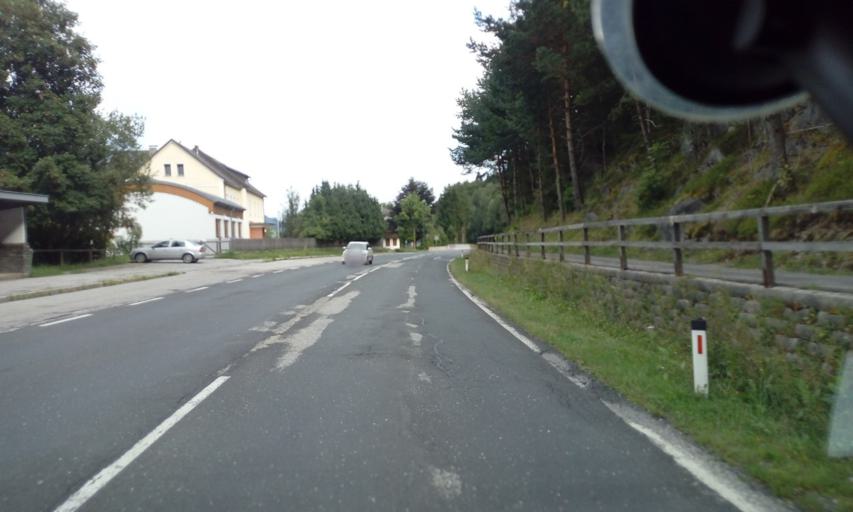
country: AT
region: Carinthia
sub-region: Politischer Bezirk Villach Land
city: Fresach
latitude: 46.6639
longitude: 13.7341
